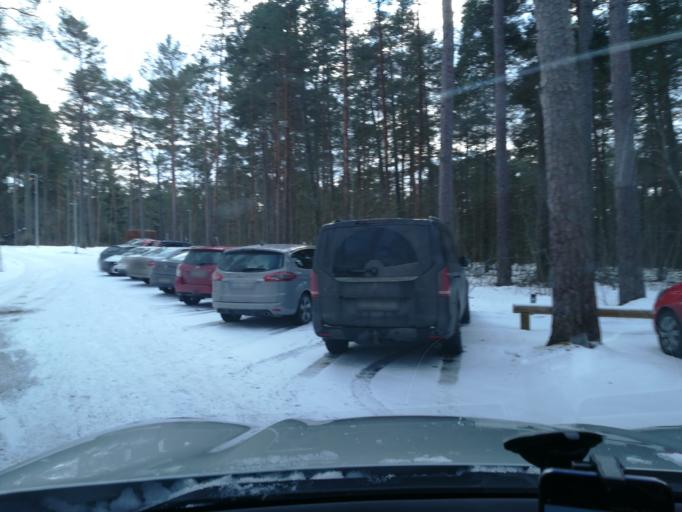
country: EE
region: Harju
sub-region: Paldiski linn
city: Paldiski
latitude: 59.3819
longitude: 24.2330
